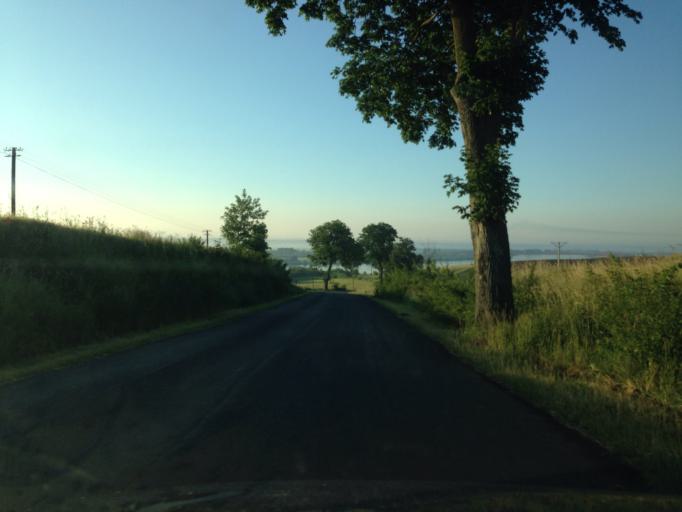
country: PL
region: Pomeranian Voivodeship
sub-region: Powiat tczewski
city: Gniew
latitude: 53.7821
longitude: 18.8254
